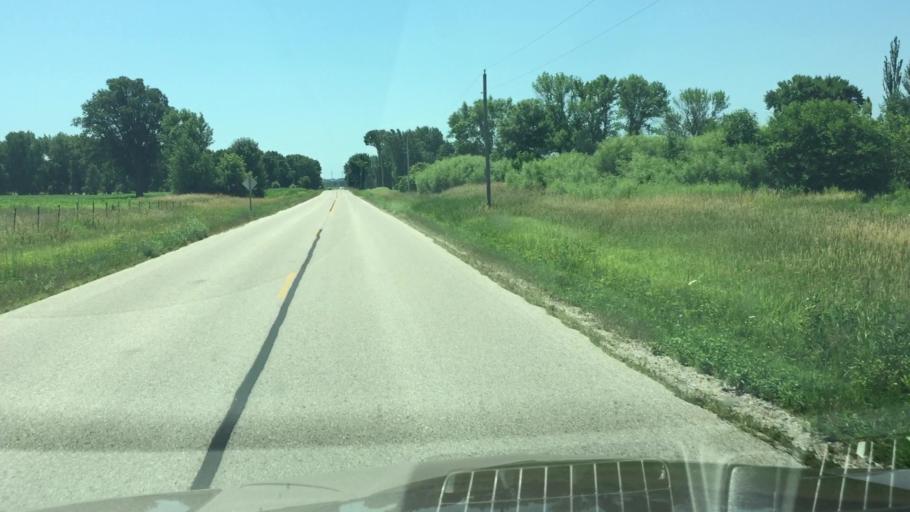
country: US
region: Wisconsin
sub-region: Fond du Lac County
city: Saint Peter
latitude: 43.9657
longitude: -88.3117
